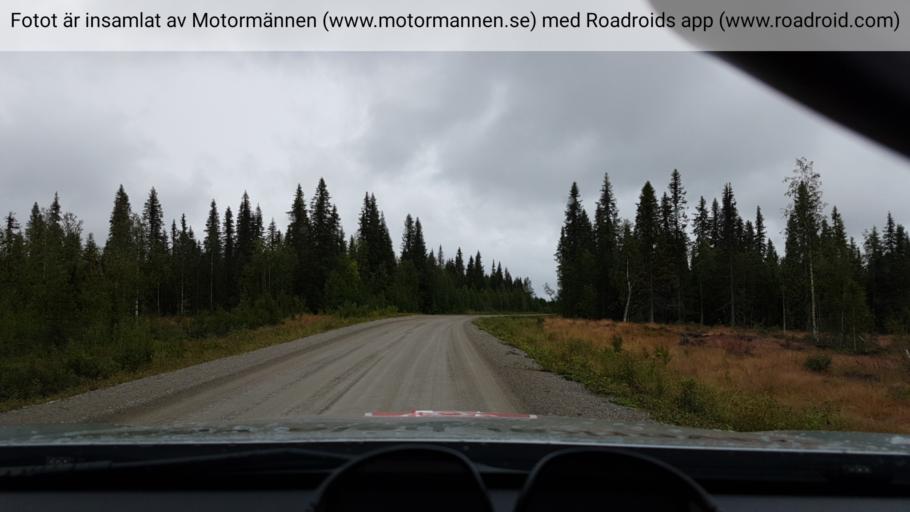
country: SE
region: Vaesterbotten
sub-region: Storumans Kommun
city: Storuman
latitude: 64.8528
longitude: 17.4039
